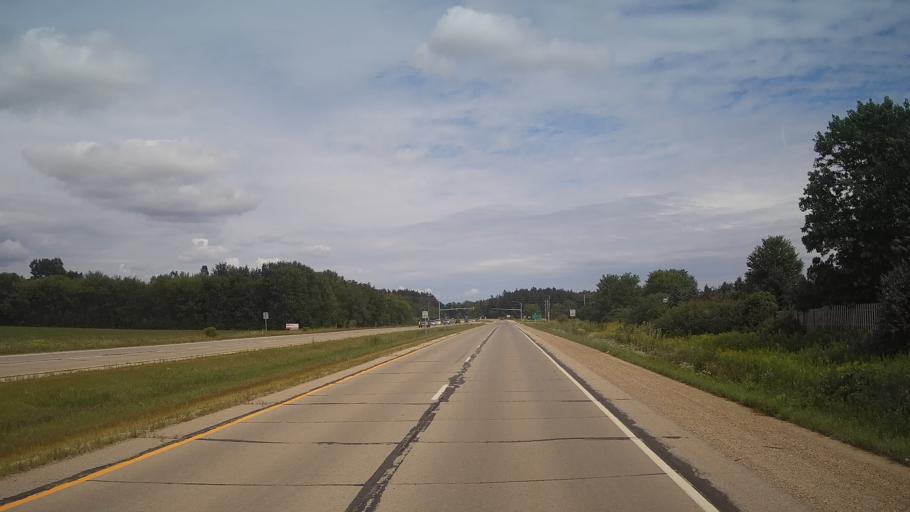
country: US
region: Wisconsin
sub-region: Winnebago County
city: Oshkosh
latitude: 44.0287
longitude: -88.6076
